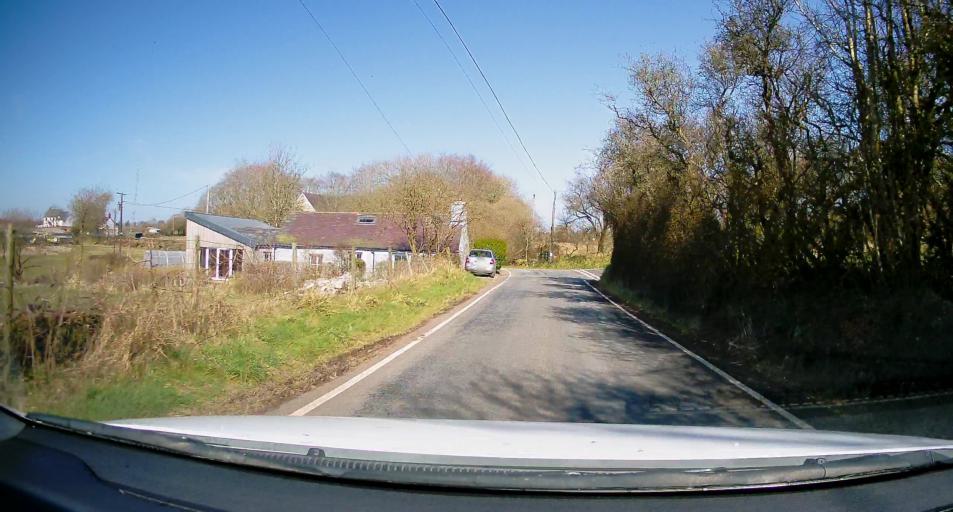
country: GB
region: Wales
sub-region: County of Ceredigion
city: Lledrod
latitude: 52.2825
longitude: -4.0599
